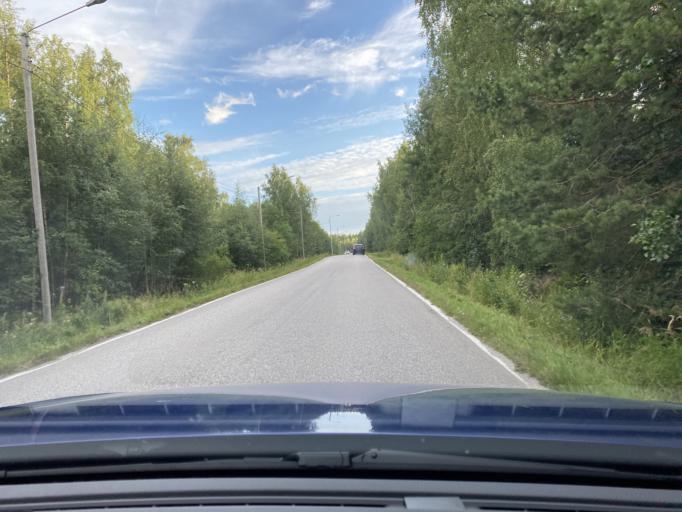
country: FI
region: Ostrobothnia
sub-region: Vaasa
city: Korsnaes
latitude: 62.9570
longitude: 21.1831
